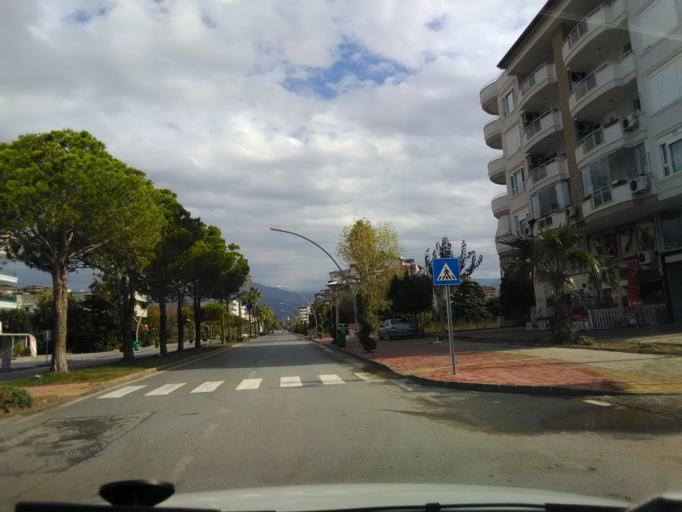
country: TR
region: Antalya
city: Gazipasa
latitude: 36.2661
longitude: 32.2982
